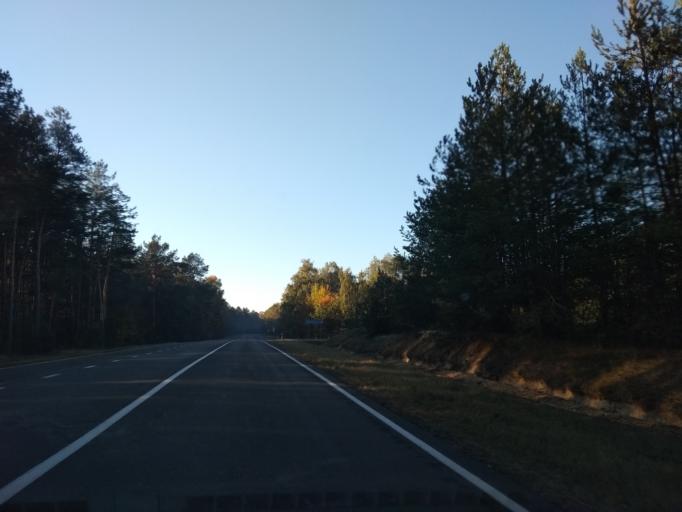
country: BY
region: Brest
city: Kobryn
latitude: 52.0376
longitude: 24.2718
